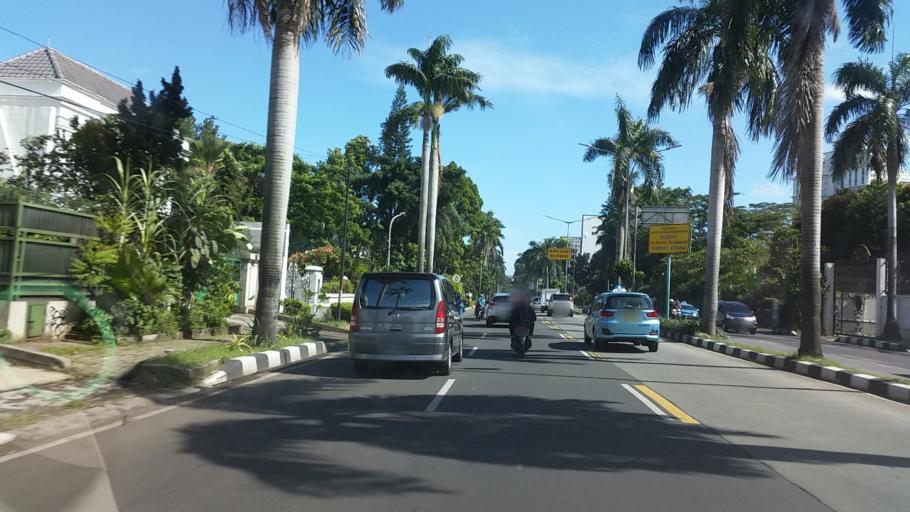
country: ID
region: Banten
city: South Tangerang
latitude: -6.2761
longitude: 106.7819
